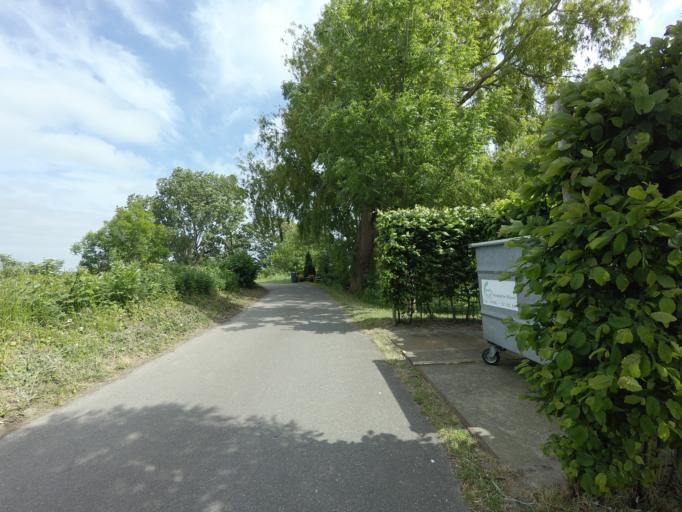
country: NL
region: South Holland
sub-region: Gemeente Spijkenisse
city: Spijkenisse
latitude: 51.7430
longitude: 4.3217
